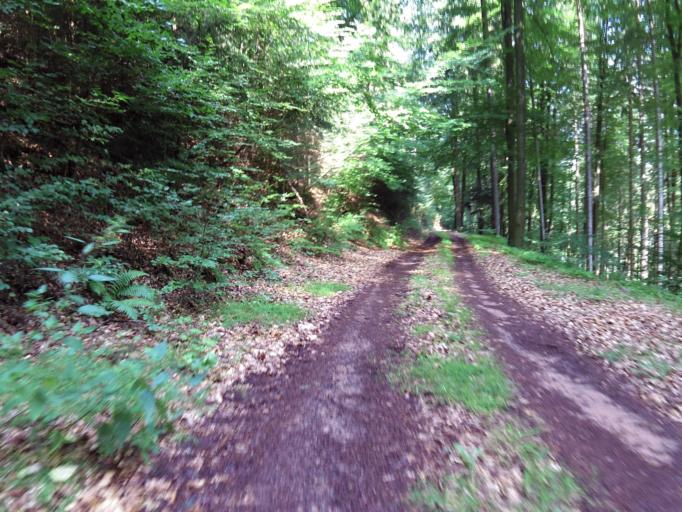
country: DE
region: Rheinland-Pfalz
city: Neidenfels
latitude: 49.4189
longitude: 8.0775
